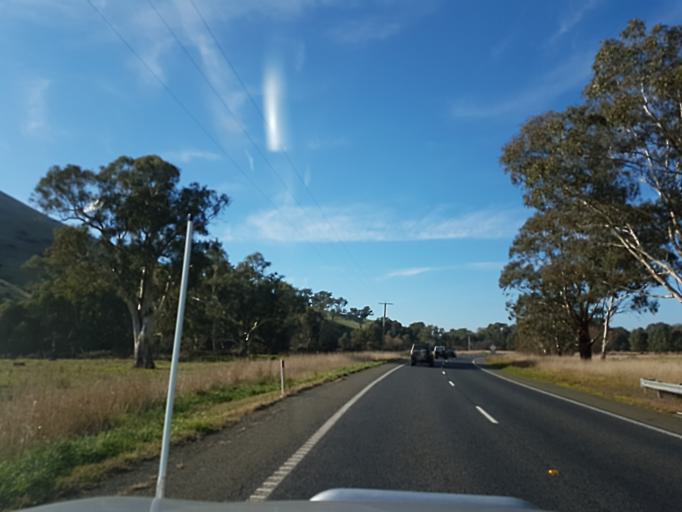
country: AU
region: Victoria
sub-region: Murrindindi
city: Alexandra
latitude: -37.1548
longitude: 145.5680
